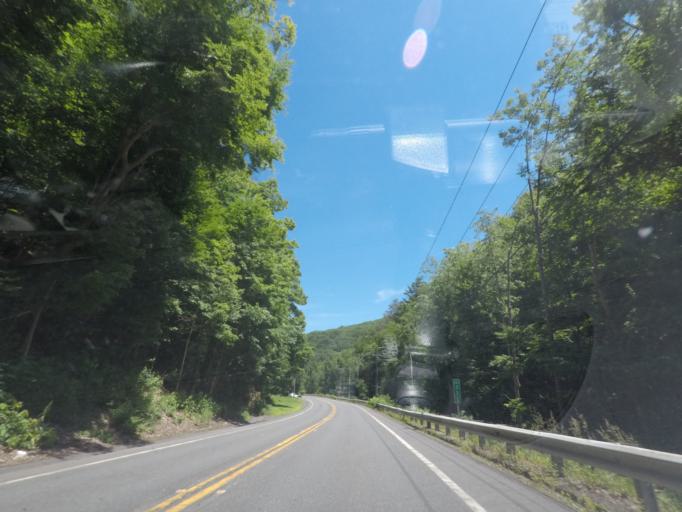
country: US
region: Massachusetts
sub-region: Berkshire County
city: Becket
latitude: 42.2699
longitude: -73.0049
